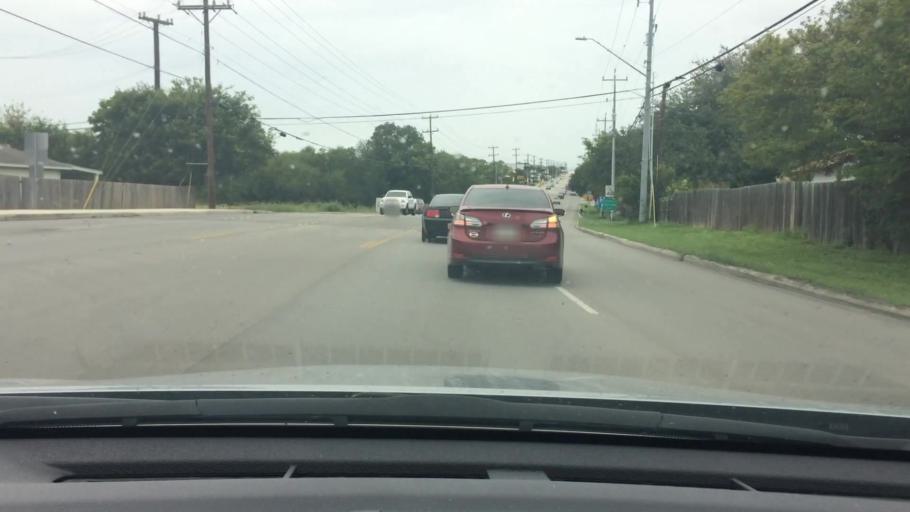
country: US
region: Texas
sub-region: Bexar County
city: Live Oak
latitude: 29.5382
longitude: -98.3367
